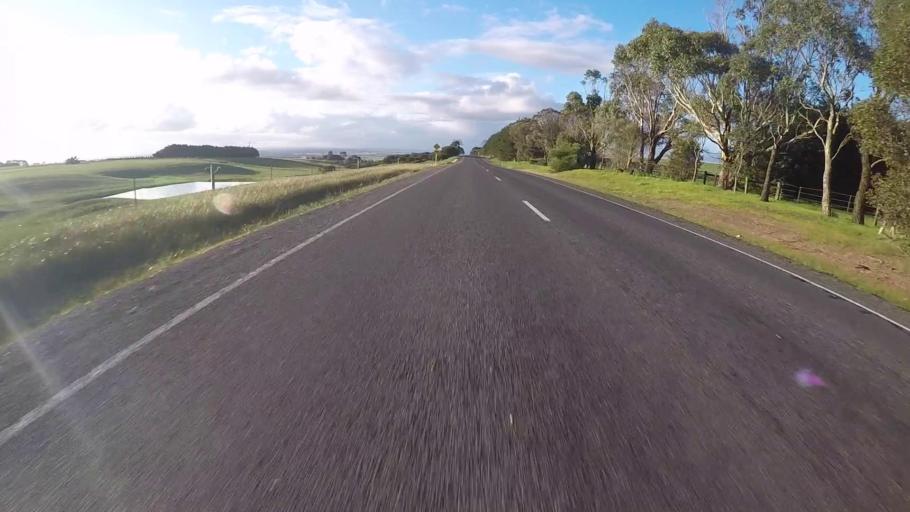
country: AU
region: Victoria
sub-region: Greater Geelong
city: Wandana Heights
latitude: -38.1650
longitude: 144.1615
